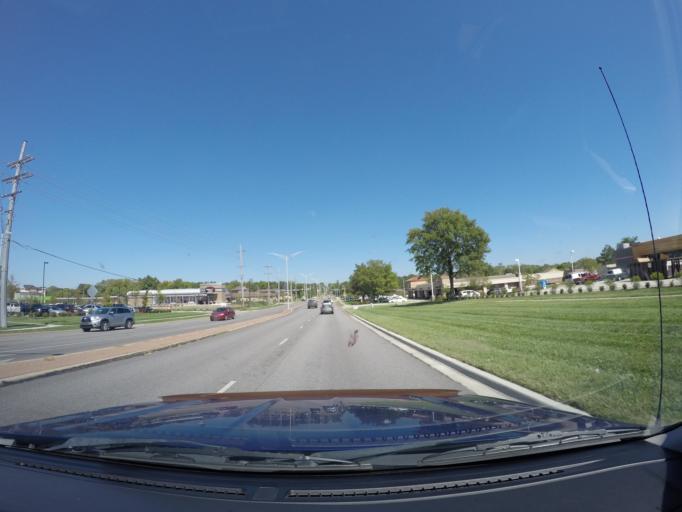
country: US
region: Kansas
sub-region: Johnson County
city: Leawood
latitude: 38.9350
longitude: -94.6395
